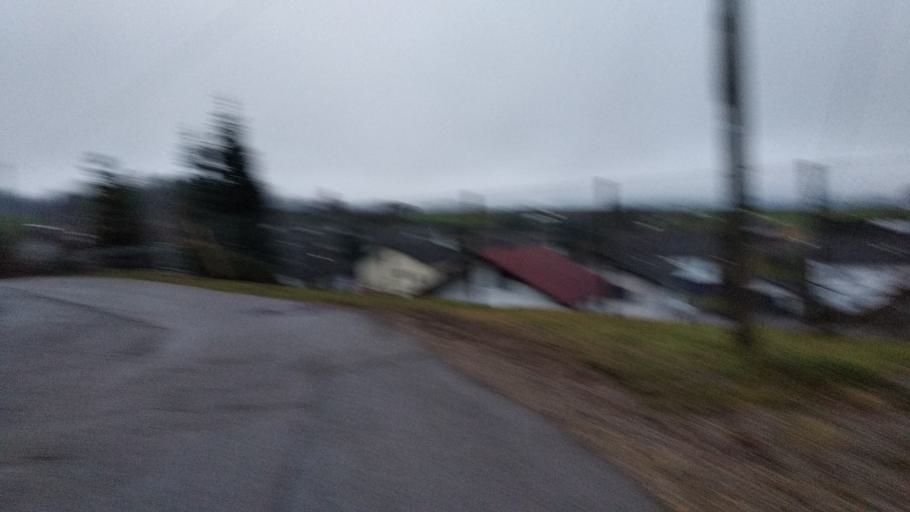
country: DE
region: Bavaria
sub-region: Swabia
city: Lautrach
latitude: 47.8874
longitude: 10.1360
